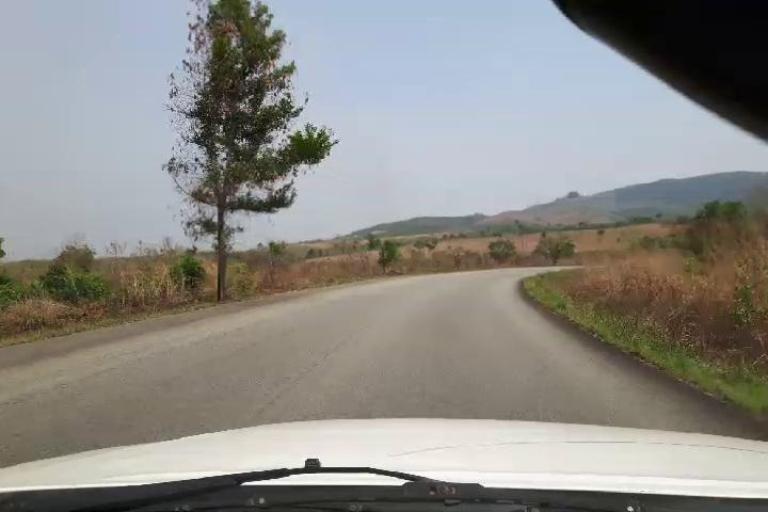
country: SL
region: Northern Province
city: Yonibana
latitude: 8.3842
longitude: -12.1940
